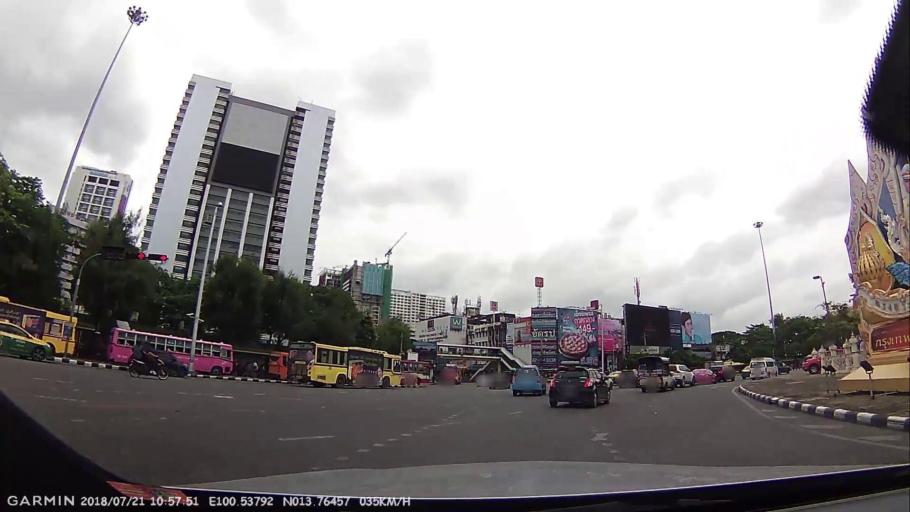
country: TH
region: Bangkok
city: Ratchathewi
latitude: 13.7646
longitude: 100.5379
